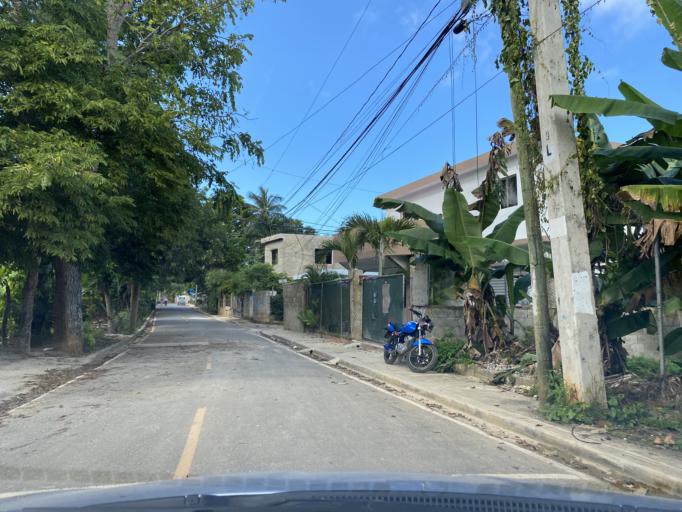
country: DO
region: Samana
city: Las Terrenas
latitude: 19.3030
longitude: -69.5409
